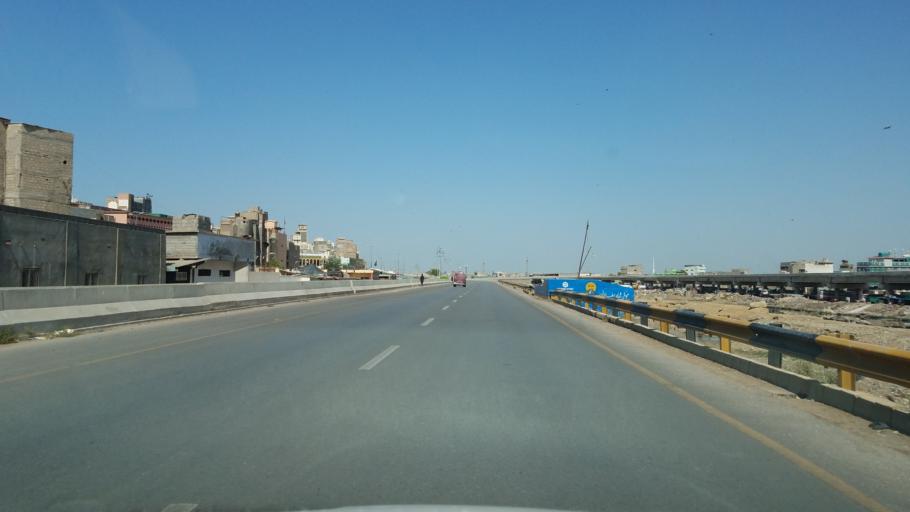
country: PK
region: Sindh
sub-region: Karachi District
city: Karachi
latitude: 24.8794
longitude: 67.0084
